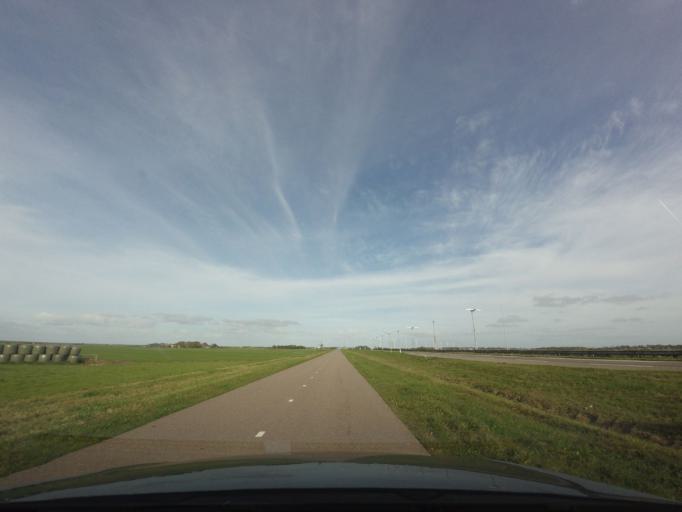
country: NL
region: North Holland
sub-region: Gemeente Schagen
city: Harenkarspel
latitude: 52.7382
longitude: 4.6865
